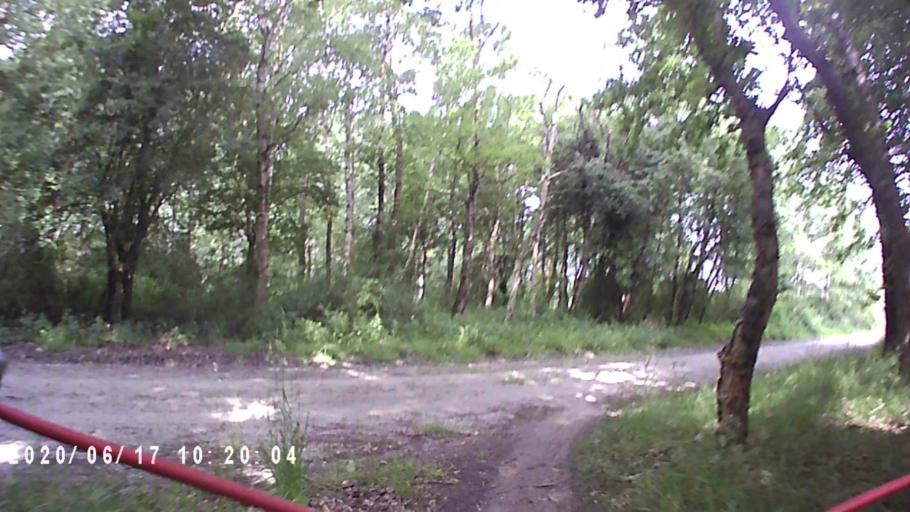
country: NL
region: Groningen
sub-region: Gemeente De Marne
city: Ulrum
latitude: 53.3889
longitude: 6.2487
